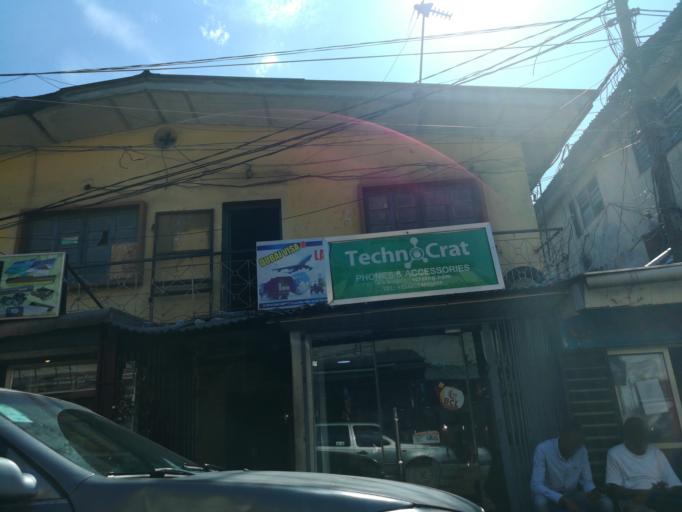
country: NG
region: Lagos
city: Ikeja
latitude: 6.5951
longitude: 3.3410
